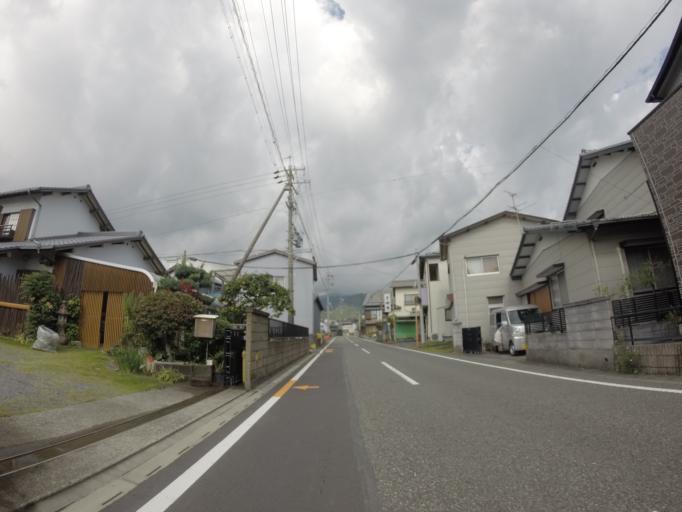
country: JP
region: Shizuoka
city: Shizuoka-shi
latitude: 35.0461
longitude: 138.4815
